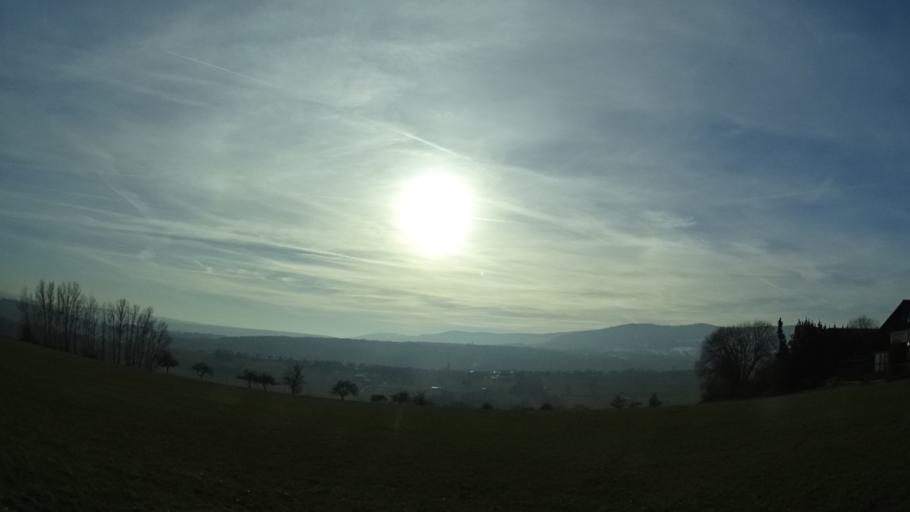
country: DE
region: Bavaria
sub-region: Regierungsbezirk Unterfranken
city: Sandberg
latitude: 50.3436
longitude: 10.0113
